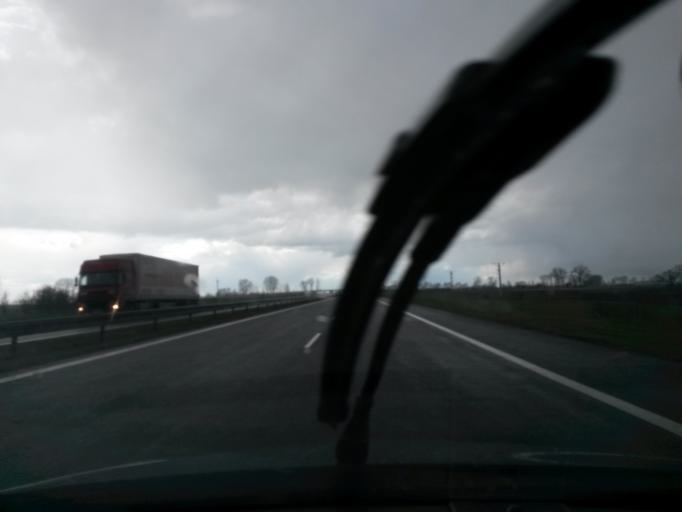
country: PL
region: Greater Poland Voivodeship
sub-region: Powiat poznanski
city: Kleszczewo
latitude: 52.3103
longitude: 17.2238
